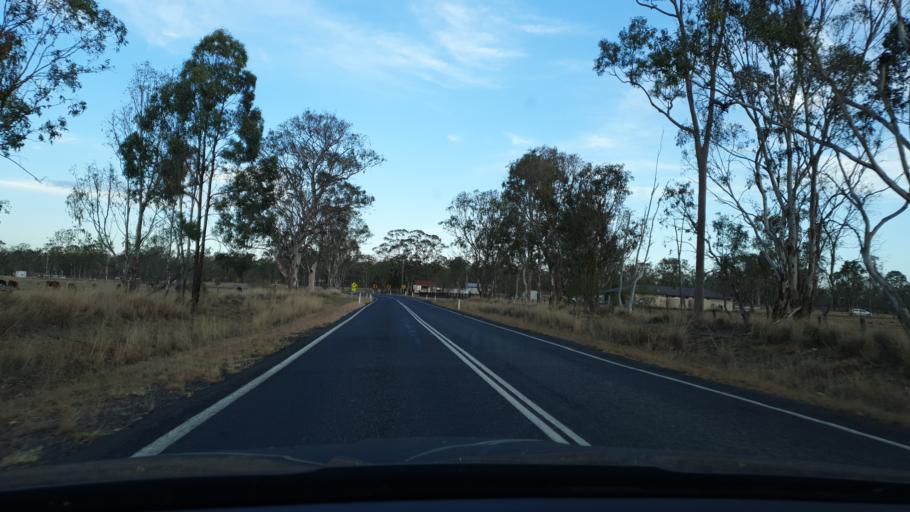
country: AU
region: Queensland
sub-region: Southern Downs
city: Warwick
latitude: -28.1080
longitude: 151.9581
